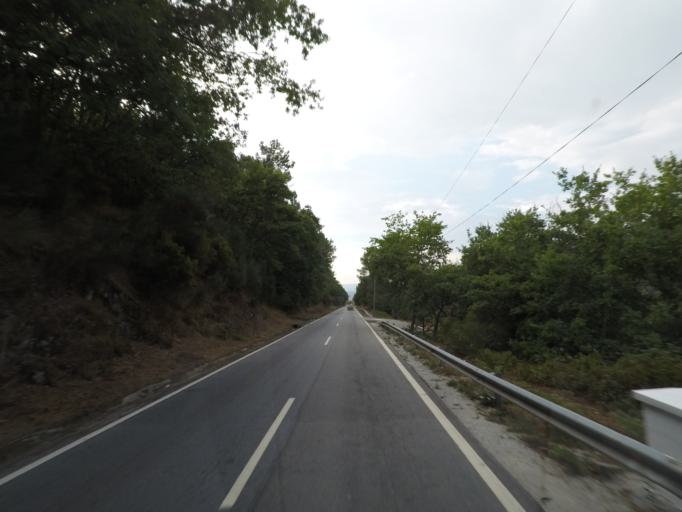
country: PT
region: Porto
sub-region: Baiao
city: Baiao
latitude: 41.2208
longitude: -7.9908
